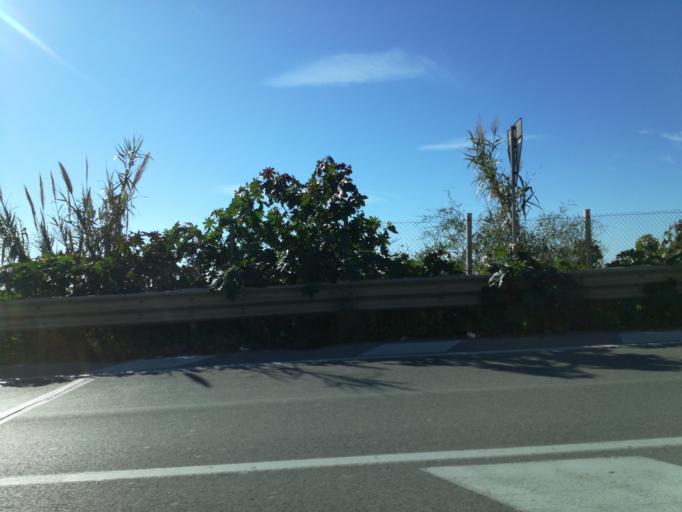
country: IT
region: Sicily
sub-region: Provincia di Caltanissetta
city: Gela
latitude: 37.0675
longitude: 14.2333
